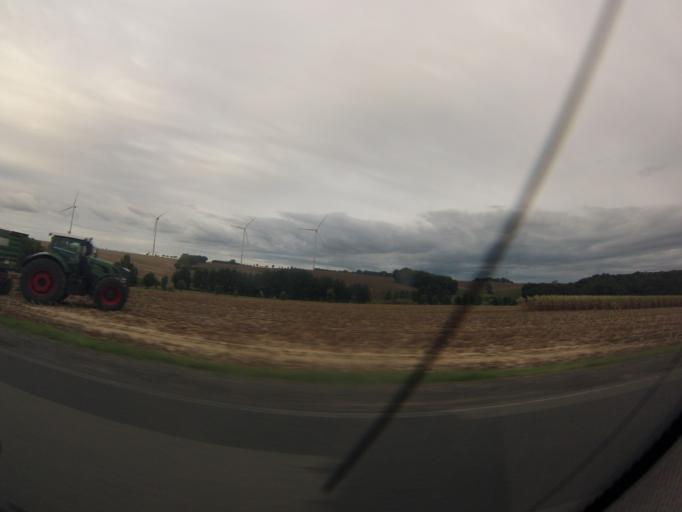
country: DE
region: Thuringia
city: Wildenborten
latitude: 50.8962
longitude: 12.2952
